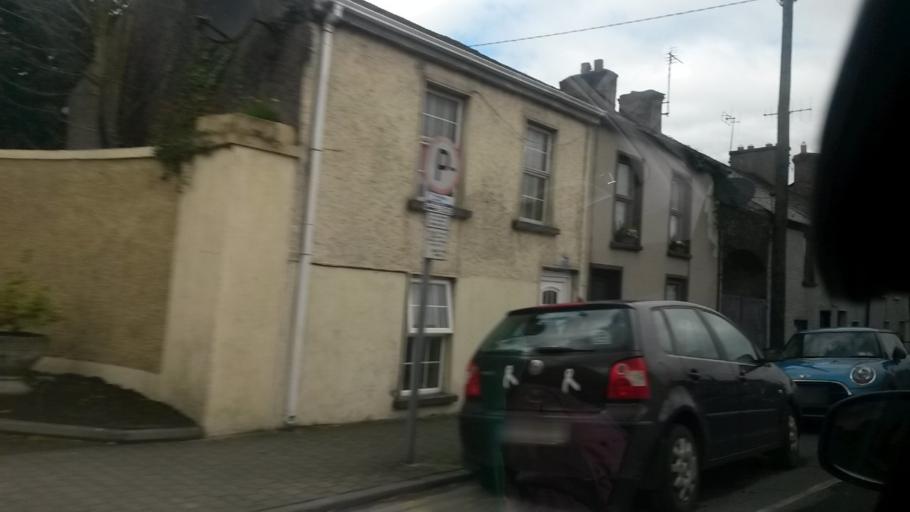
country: IE
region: Munster
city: Cashel
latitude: 52.5154
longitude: -7.8913
